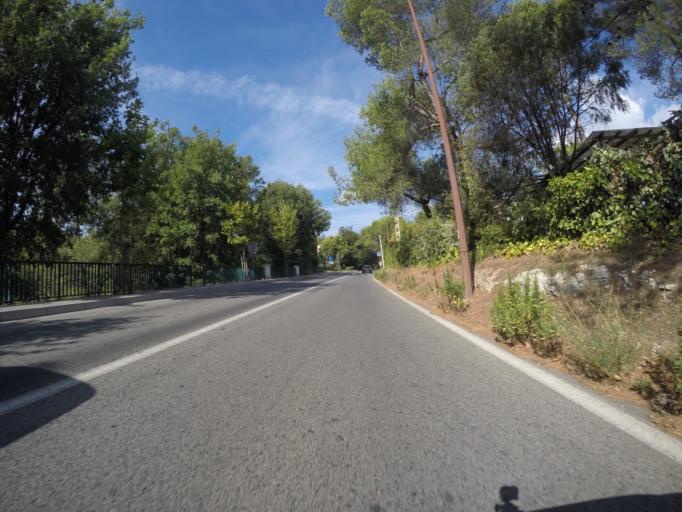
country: FR
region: Provence-Alpes-Cote d'Azur
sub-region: Departement des Alpes-Maritimes
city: Le Rouret
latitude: 43.6732
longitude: 6.9991
